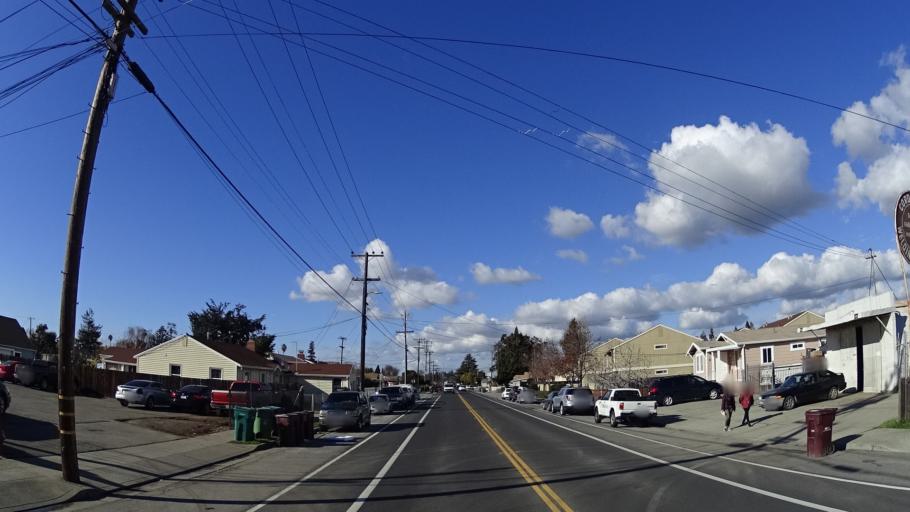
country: US
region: California
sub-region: Alameda County
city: Cherryland
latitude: 37.6783
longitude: -122.1115
